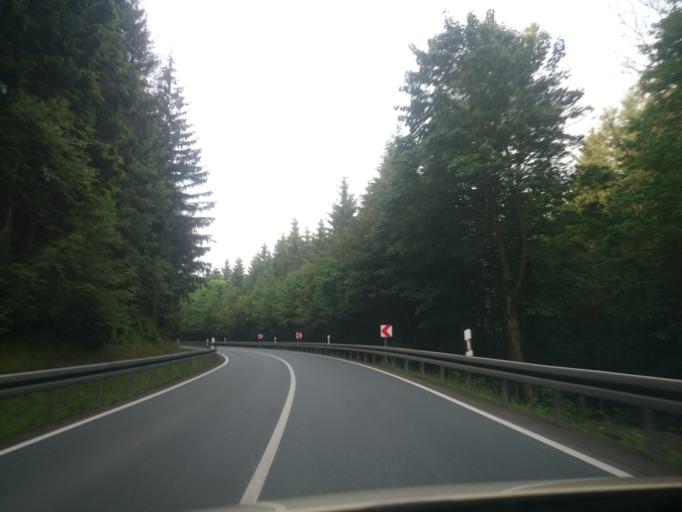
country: DE
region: Saxony
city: Marienberg
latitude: 50.6951
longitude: 13.1487
